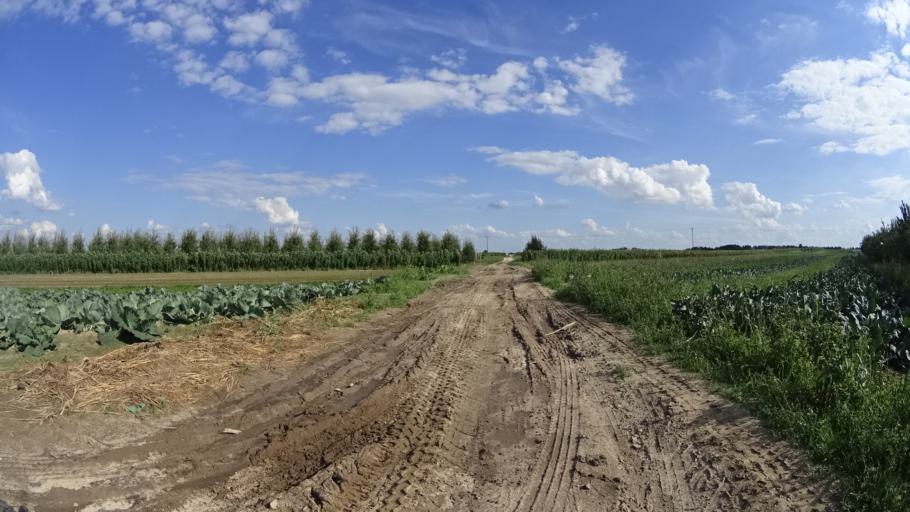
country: PL
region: Masovian Voivodeship
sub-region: Powiat bialobrzeski
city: Wysmierzyce
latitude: 51.6645
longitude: 20.8143
